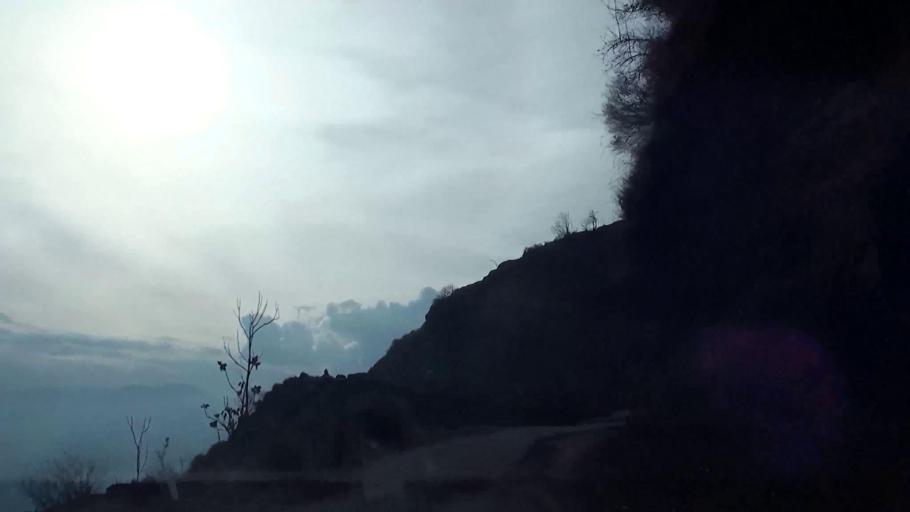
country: PK
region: Azad Kashmir
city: Muzaffarabad
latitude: 34.3695
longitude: 73.5193
